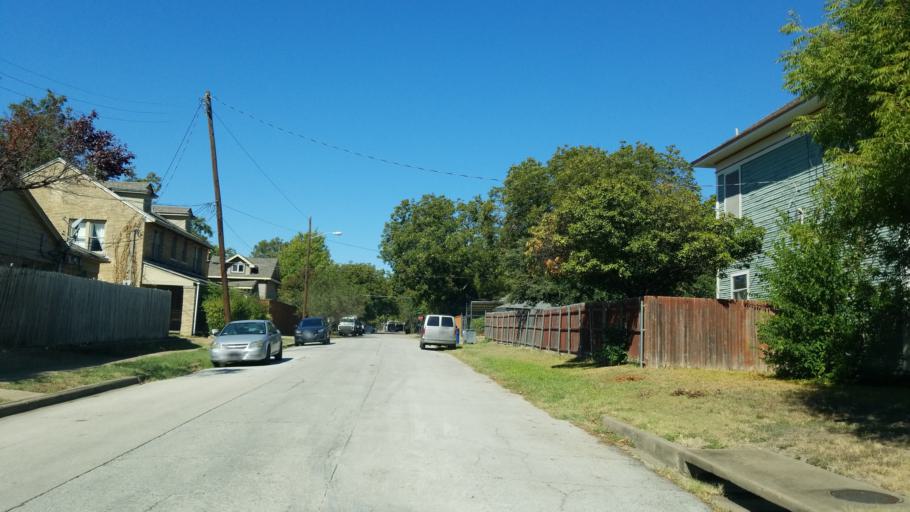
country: US
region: Texas
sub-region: Dallas County
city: Highland Park
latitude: 32.8046
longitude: -96.7577
